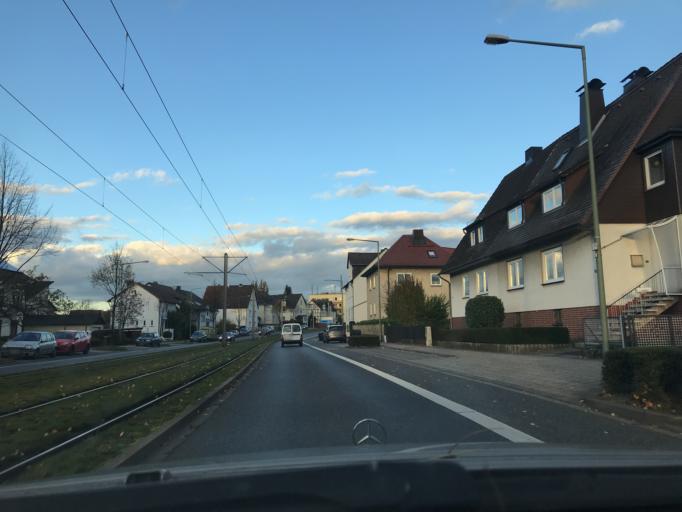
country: DE
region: Hesse
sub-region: Regierungsbezirk Kassel
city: Fuldabruck
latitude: 51.2810
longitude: 9.4613
